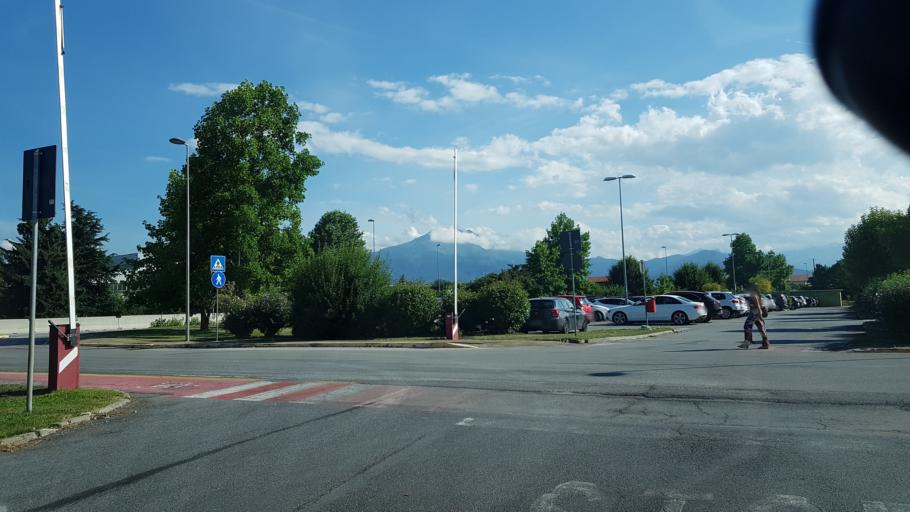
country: IT
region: Piedmont
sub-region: Provincia di Cuneo
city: Cuneo
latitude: 44.3916
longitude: 7.5841
